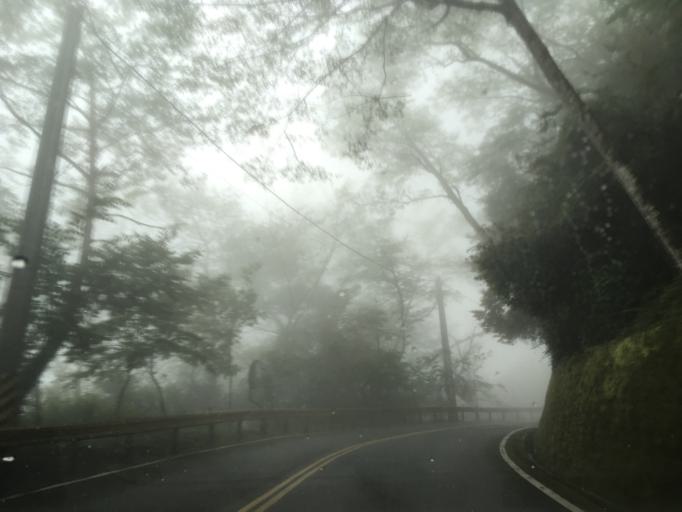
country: TW
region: Taiwan
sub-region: Hualien
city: Hualian
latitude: 24.1929
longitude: 121.4186
